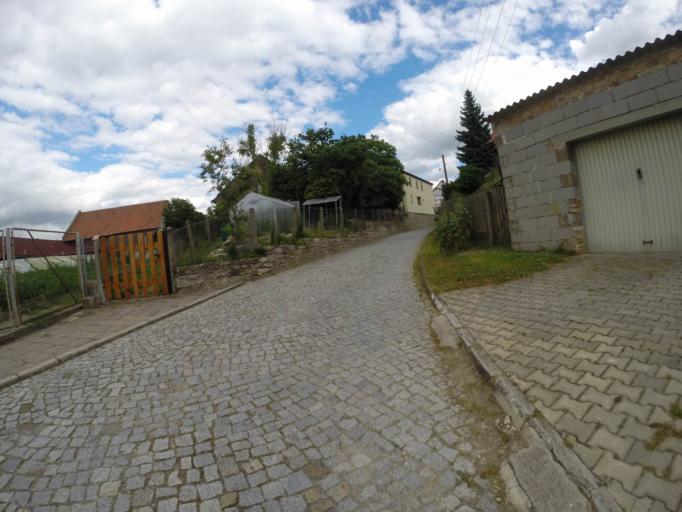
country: DE
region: Thuringia
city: Grosslobichau
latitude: 50.9276
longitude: 11.6770
